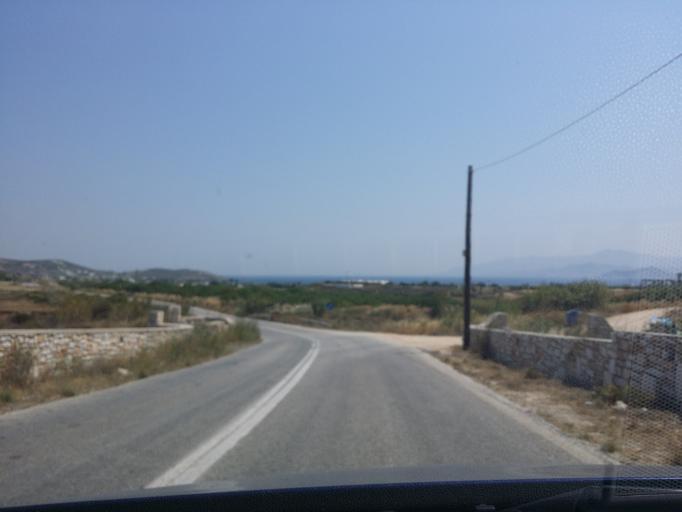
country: GR
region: South Aegean
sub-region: Nomos Kykladon
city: Naousa
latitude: 37.0686
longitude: 25.2441
